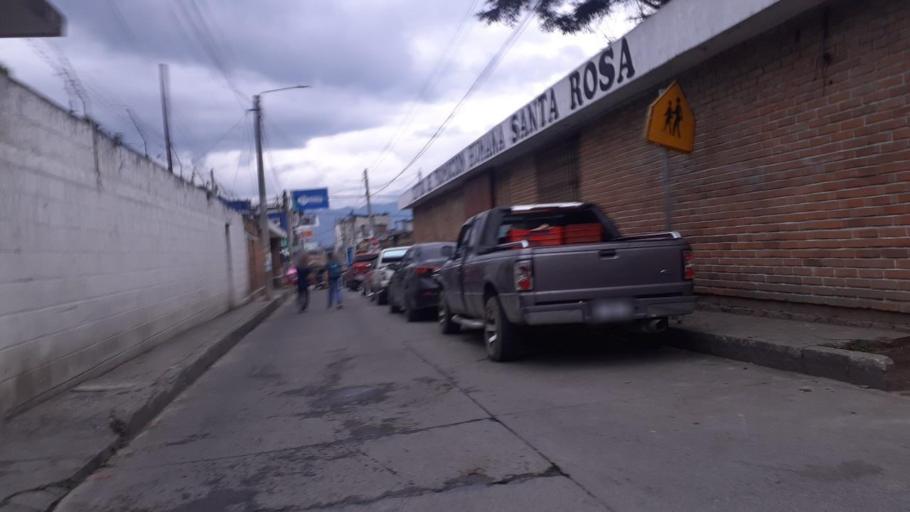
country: GT
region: Quetzaltenango
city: Ostuncalco
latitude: 14.8691
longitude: -91.6204
